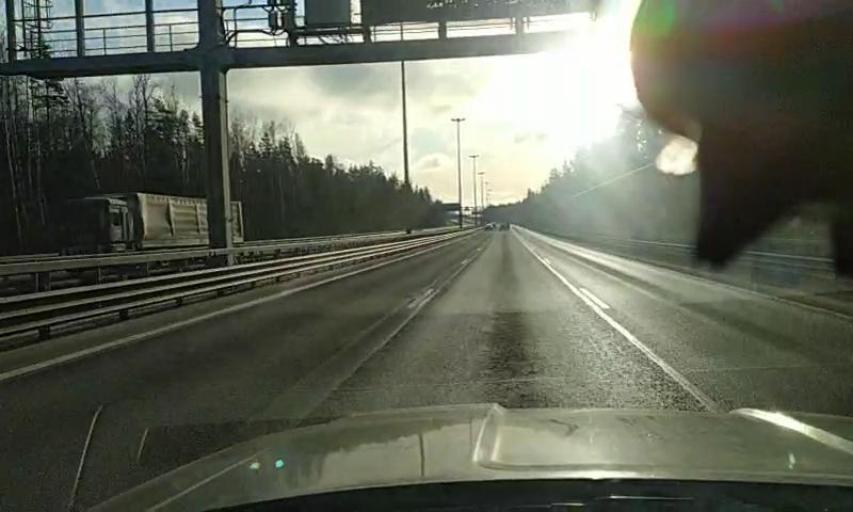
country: RU
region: St.-Petersburg
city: Beloostrov
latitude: 60.1227
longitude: 30.0703
